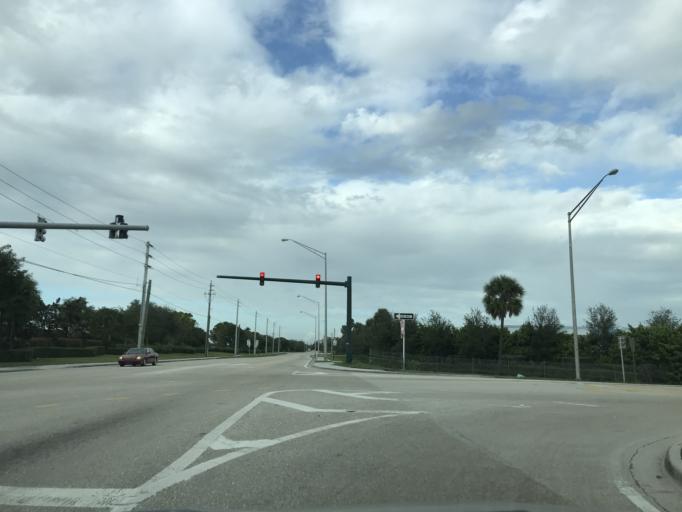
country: US
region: Florida
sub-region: Palm Beach County
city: Lake Belvedere Estates
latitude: 26.6850
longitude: -80.1658
